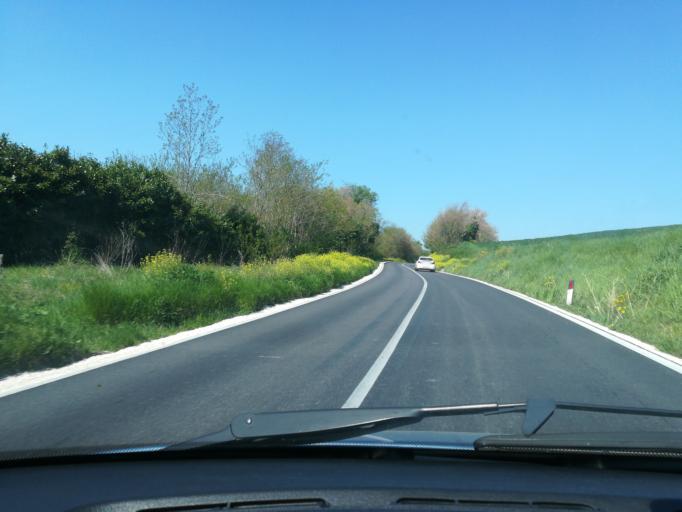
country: IT
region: The Marches
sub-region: Provincia di Macerata
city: Villa Potenza
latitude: 43.3286
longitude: 13.3922
